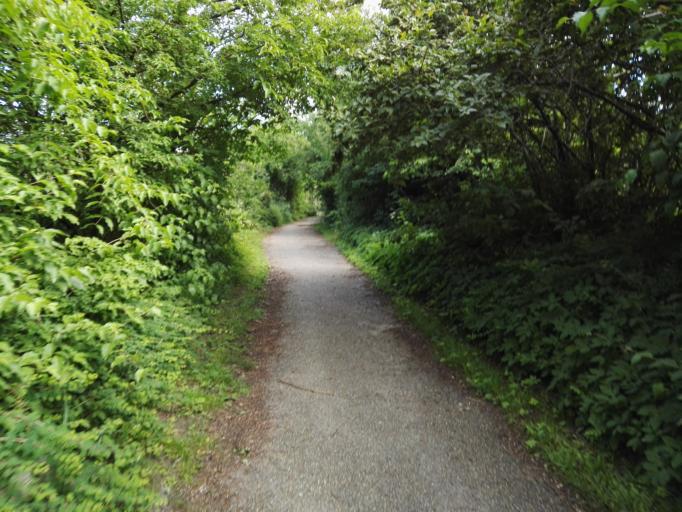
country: DK
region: Capital Region
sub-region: Herlev Kommune
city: Herlev
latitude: 55.7355
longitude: 12.4092
